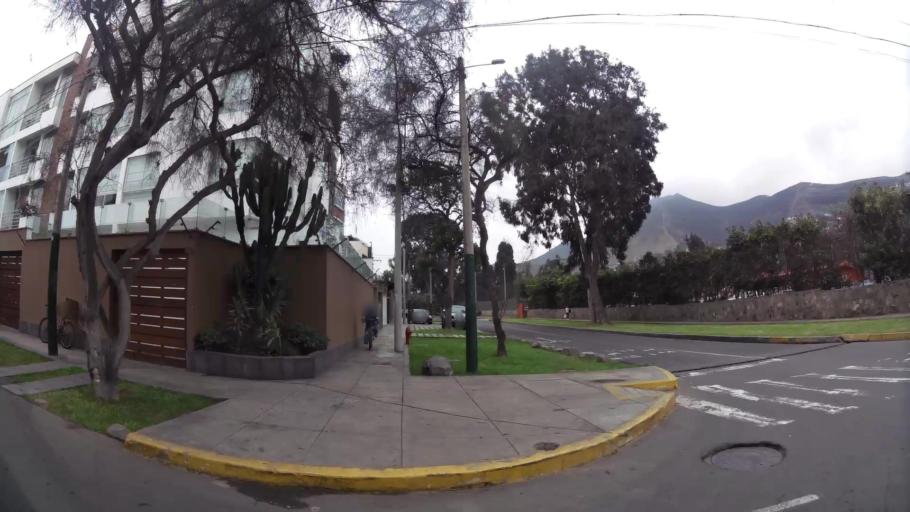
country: PE
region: Lima
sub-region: Lima
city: La Molina
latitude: -12.1172
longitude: -76.9720
